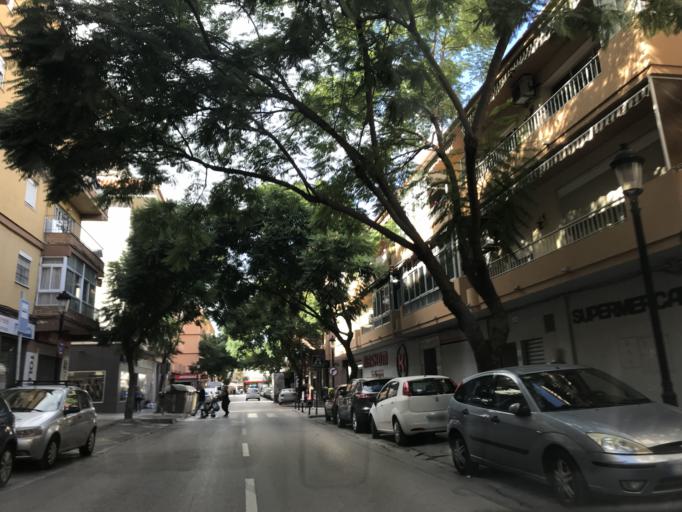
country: ES
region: Andalusia
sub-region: Provincia de Malaga
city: Fuengirola
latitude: 36.5397
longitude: -4.6292
